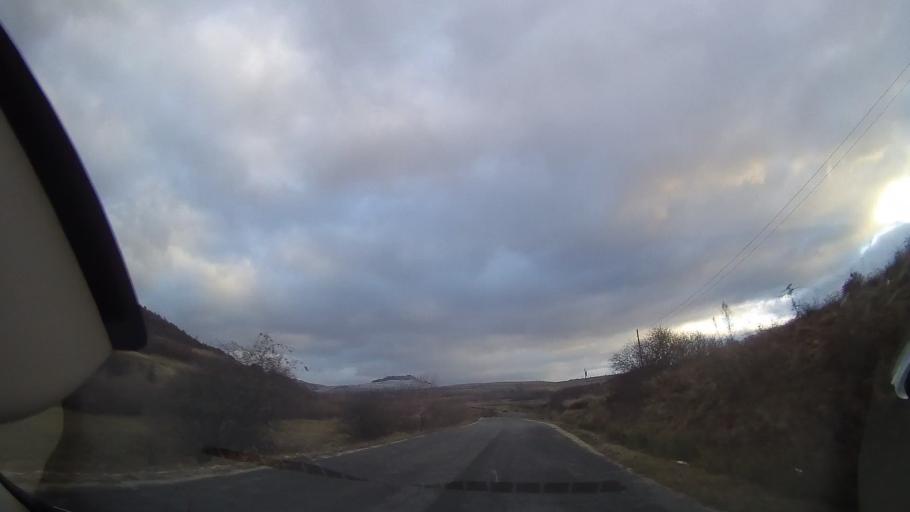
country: RO
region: Cluj
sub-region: Comuna Calatele
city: Calatele
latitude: 46.7882
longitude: 23.0123
